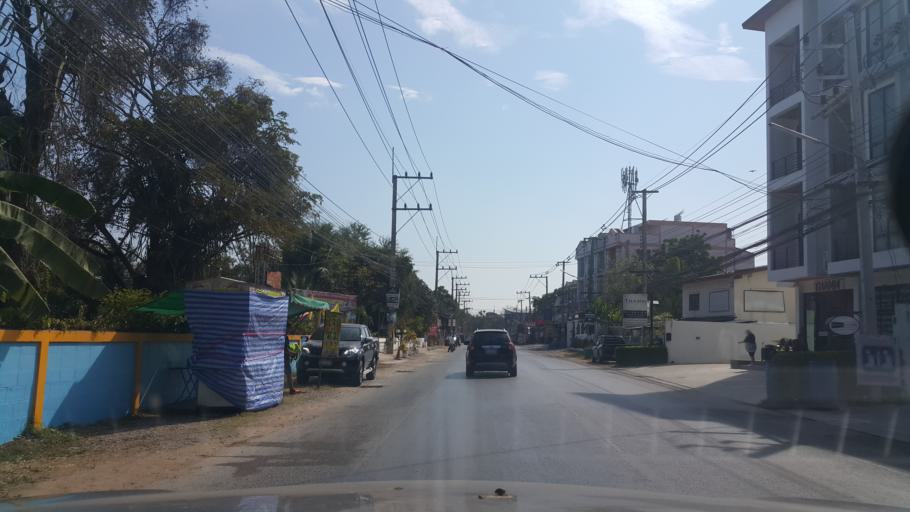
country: TH
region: Nakhon Ratchasima
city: Nakhon Ratchasima
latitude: 14.9478
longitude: 102.0510
